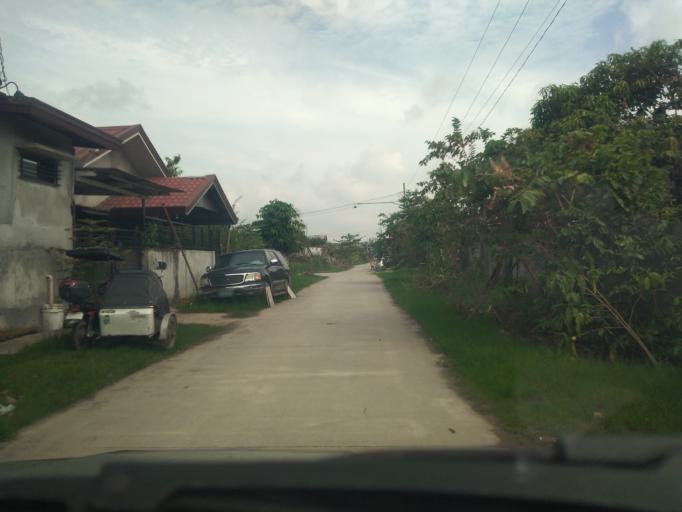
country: PH
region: Central Luzon
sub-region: Province of Pampanga
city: Pau
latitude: 15.0028
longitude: 120.7128
